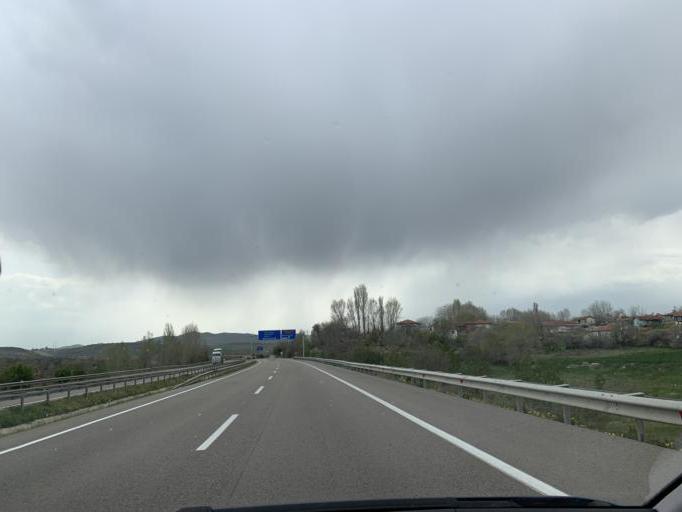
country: TR
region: Eskisehir
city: Sivrihisar
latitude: 39.5318
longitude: 31.6324
